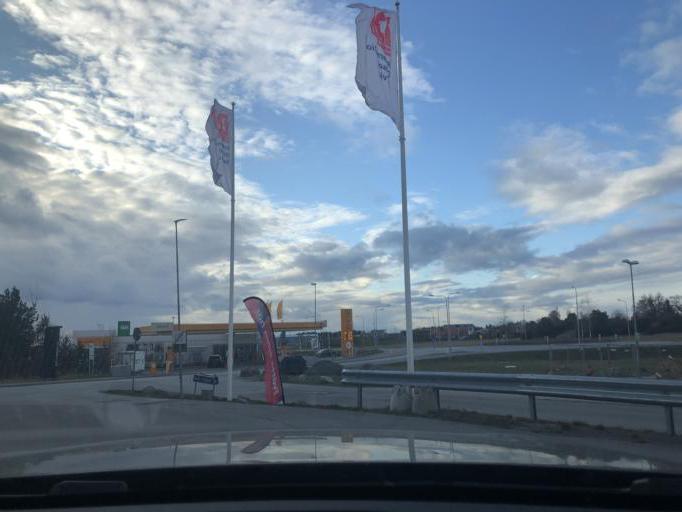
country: SE
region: Uppsala
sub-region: Uppsala Kommun
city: Saevja
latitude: 59.8443
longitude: 17.7290
